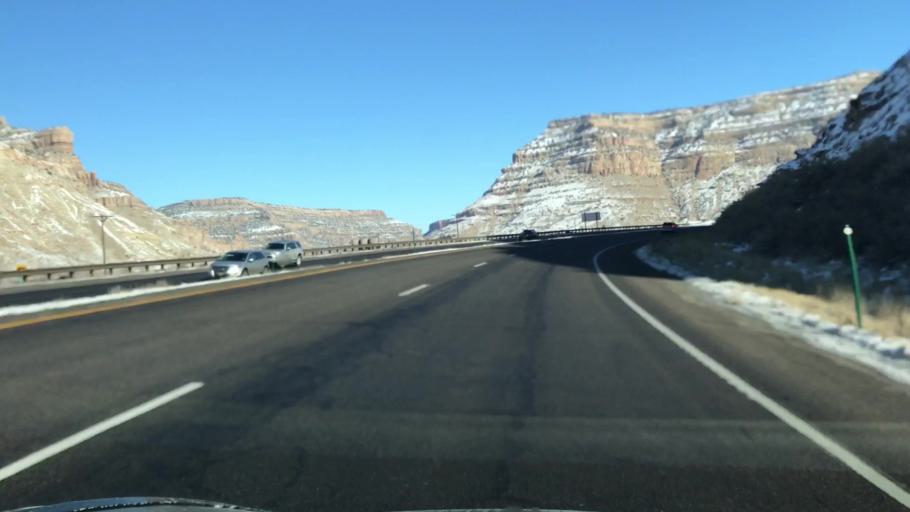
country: US
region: Colorado
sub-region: Mesa County
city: Palisade
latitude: 39.1473
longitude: -108.3130
